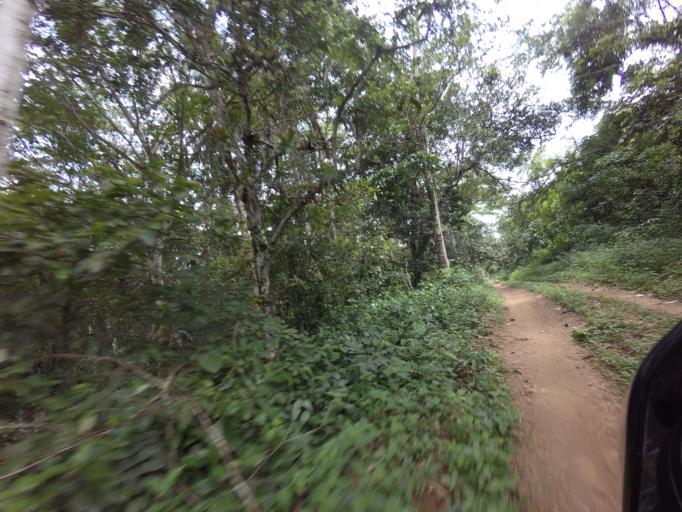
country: SL
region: Eastern Province
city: Tombodu
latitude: 8.1703
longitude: -10.6115
